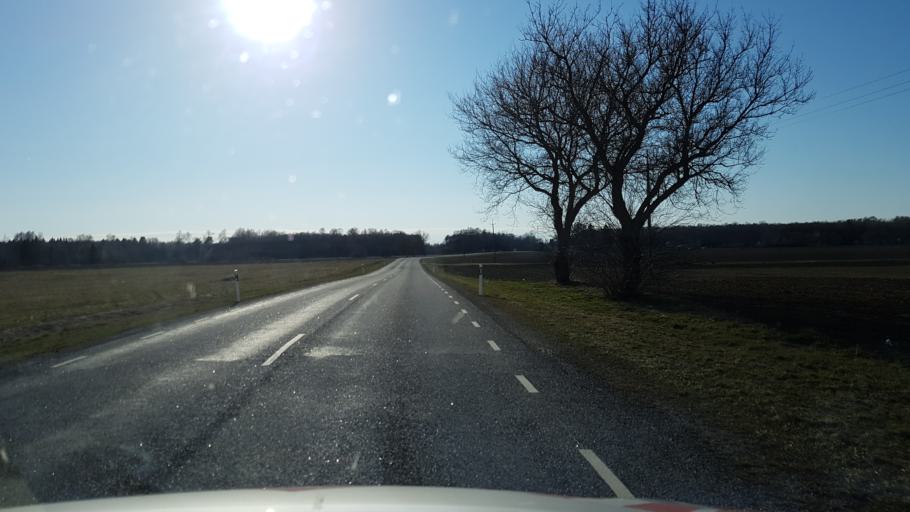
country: EE
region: Ida-Virumaa
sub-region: Kohtla-Jaerve linn
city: Kohtla-Jarve
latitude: 59.3357
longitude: 27.3178
